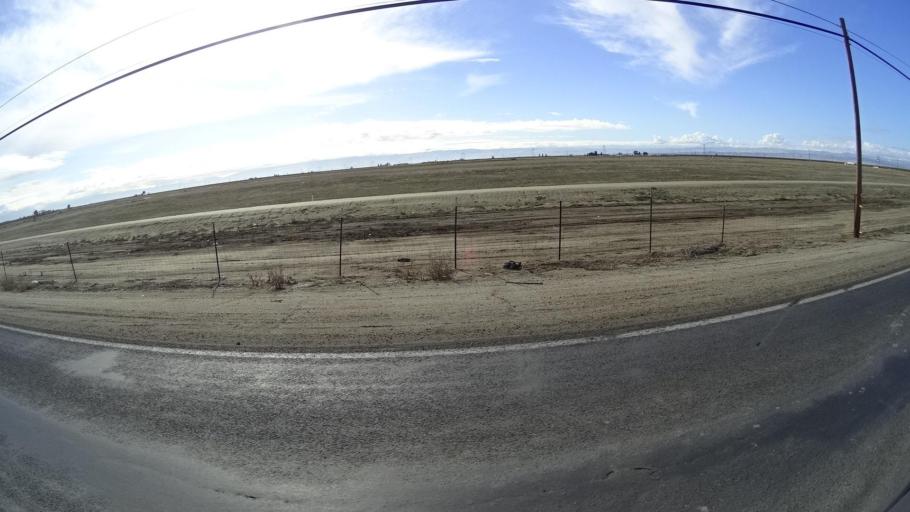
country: US
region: California
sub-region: Kern County
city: Rosedale
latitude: 35.3835
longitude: -119.2466
